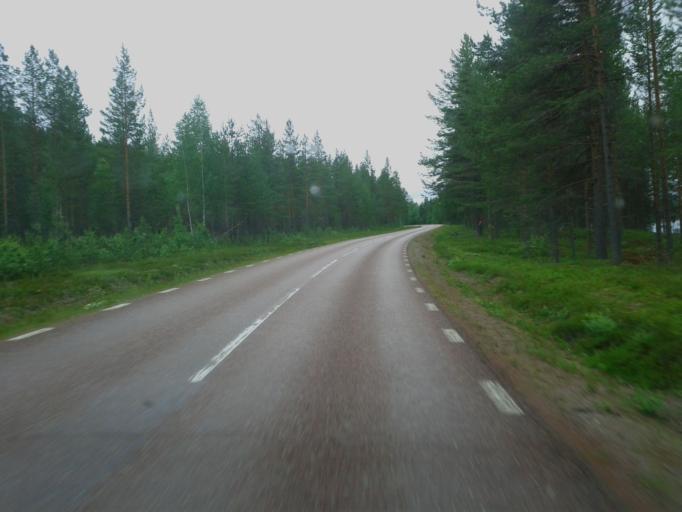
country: NO
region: Hedmark
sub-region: Trysil
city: Innbygda
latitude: 61.7887
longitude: 12.9292
